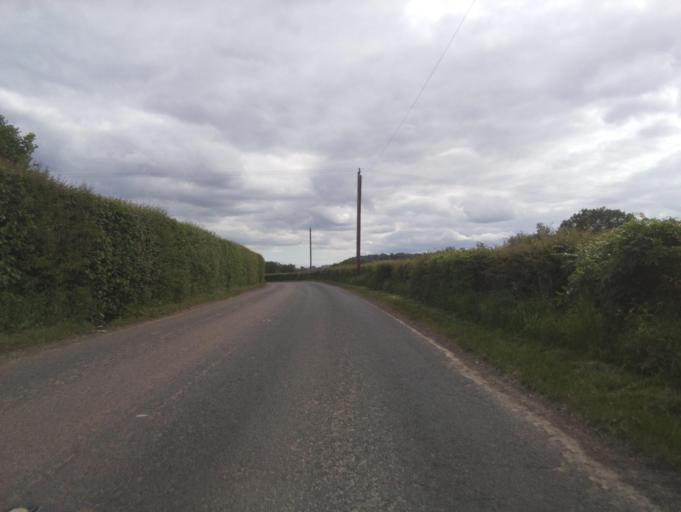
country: GB
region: England
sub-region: Herefordshire
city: Ledbury
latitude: 52.0594
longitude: -2.4430
